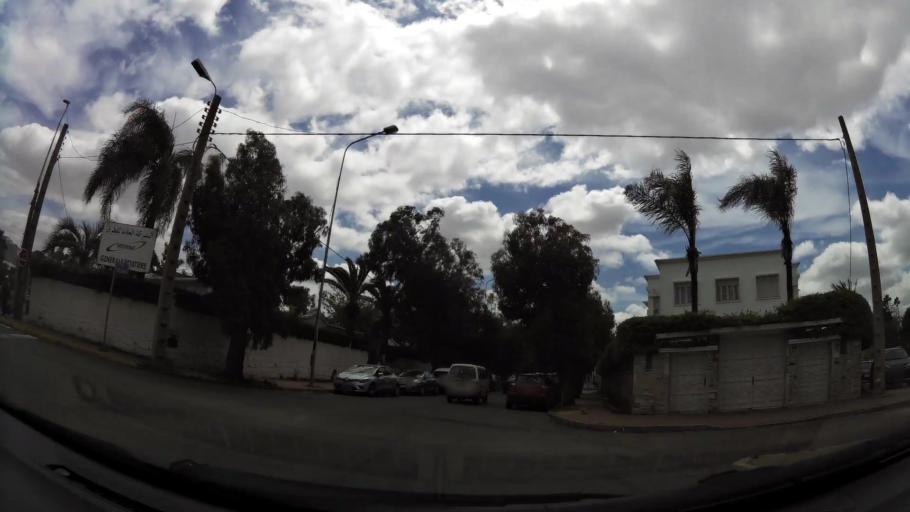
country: MA
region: Grand Casablanca
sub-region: Casablanca
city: Casablanca
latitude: 33.5618
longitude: -7.6197
